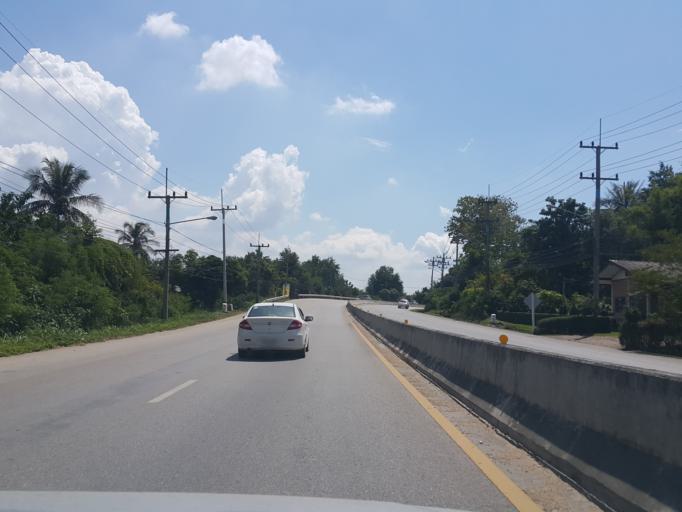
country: TH
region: Chiang Mai
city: Mae Taeng
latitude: 19.0610
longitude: 98.9414
